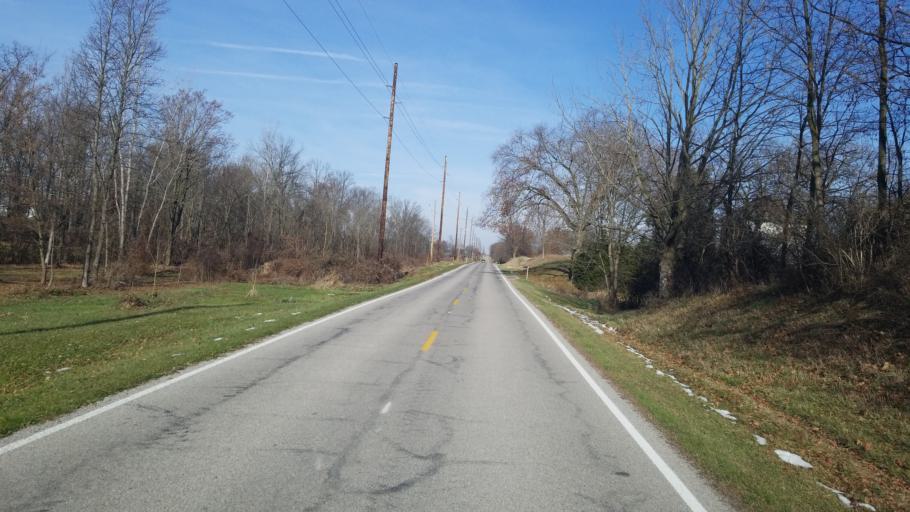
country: US
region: Ohio
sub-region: Huron County
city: Willard
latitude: 41.1447
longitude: -82.6871
